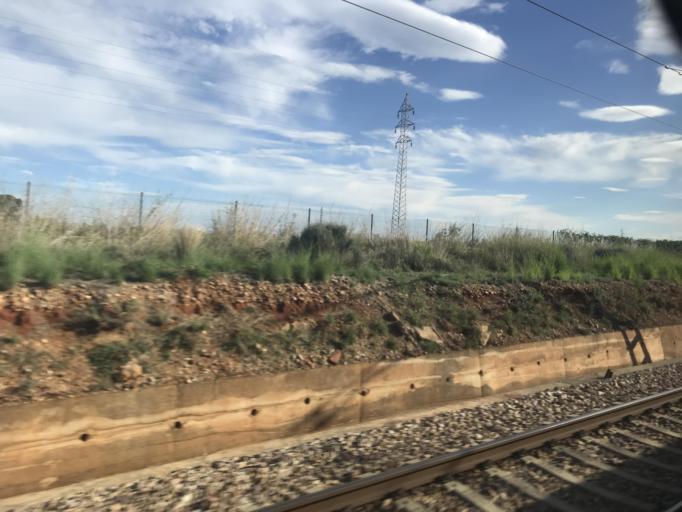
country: ES
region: Valencia
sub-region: Provincia de Castello
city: Torreblanca
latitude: 40.2238
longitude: 0.2112
